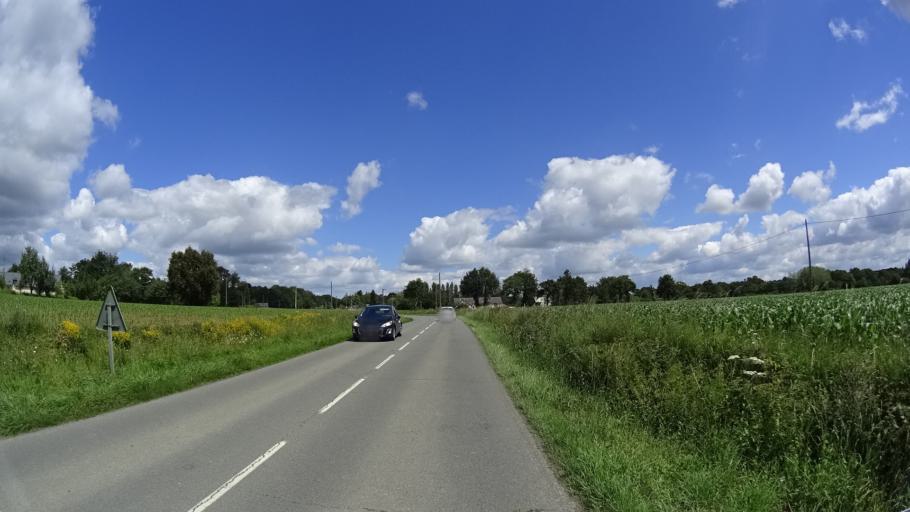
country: FR
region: Brittany
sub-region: Departement d'Ille-et-Vilaine
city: Saint-Gilles
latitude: 48.1430
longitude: -1.8289
